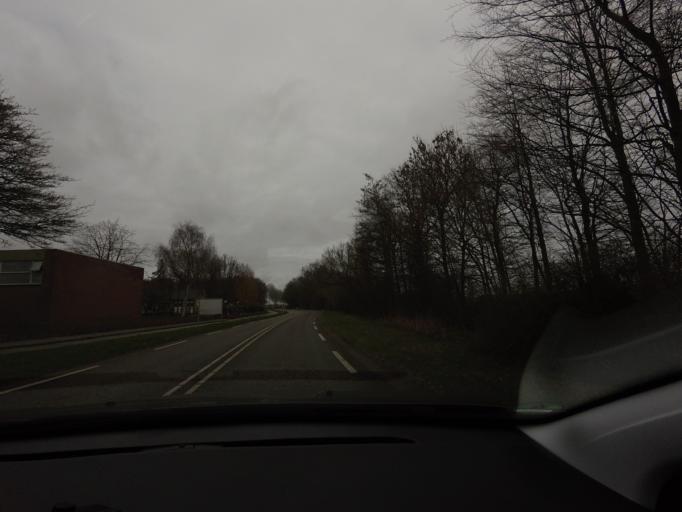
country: NL
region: Flevoland
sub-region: Gemeente Urk
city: Urk
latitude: 52.7255
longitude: 5.6457
